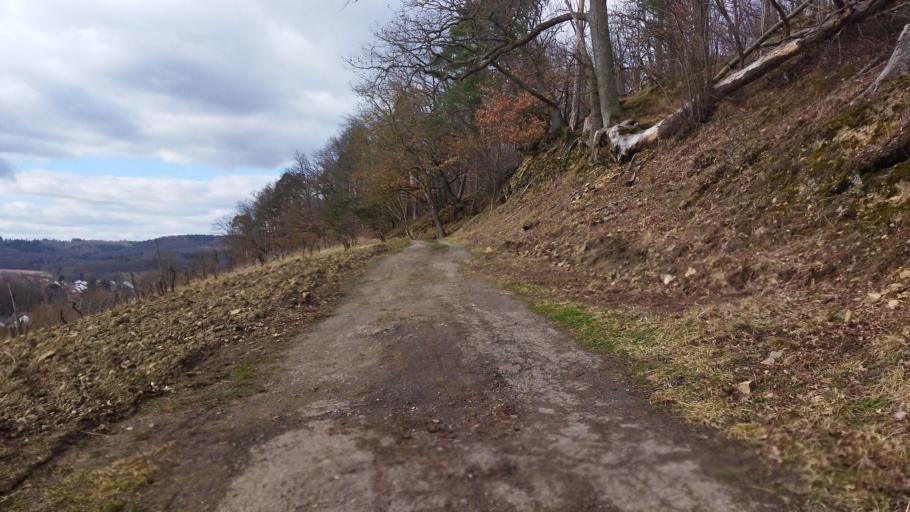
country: DE
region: Baden-Wuerttemberg
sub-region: Regierungsbezirk Stuttgart
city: Freudental
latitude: 49.0084
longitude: 9.0722
